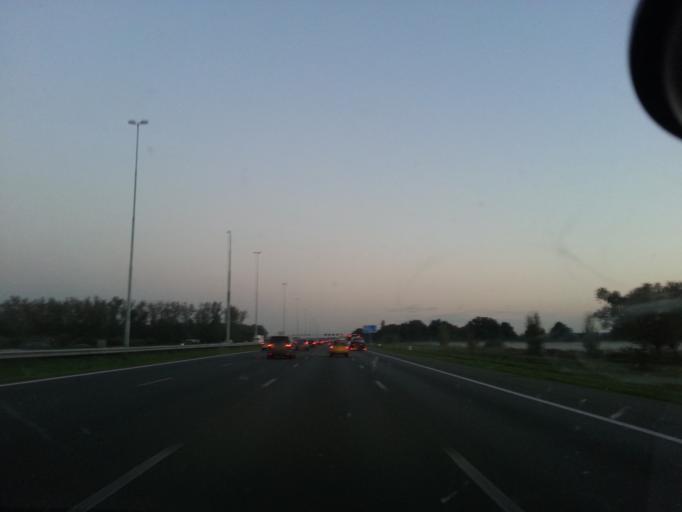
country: NL
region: Utrecht
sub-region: Gemeente Vianen
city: Vianen
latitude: 51.9615
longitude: 5.1175
